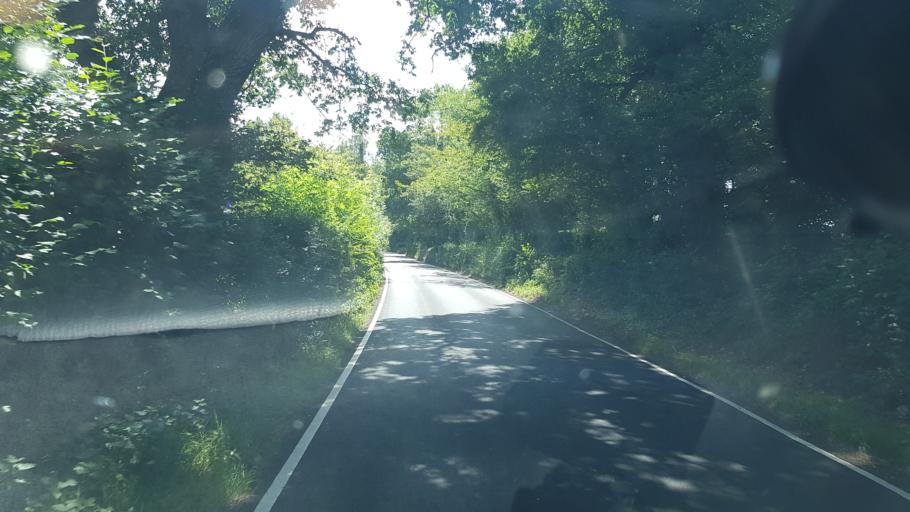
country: GB
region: England
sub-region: Kent
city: Edenbridge
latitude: 51.2228
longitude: 0.1293
